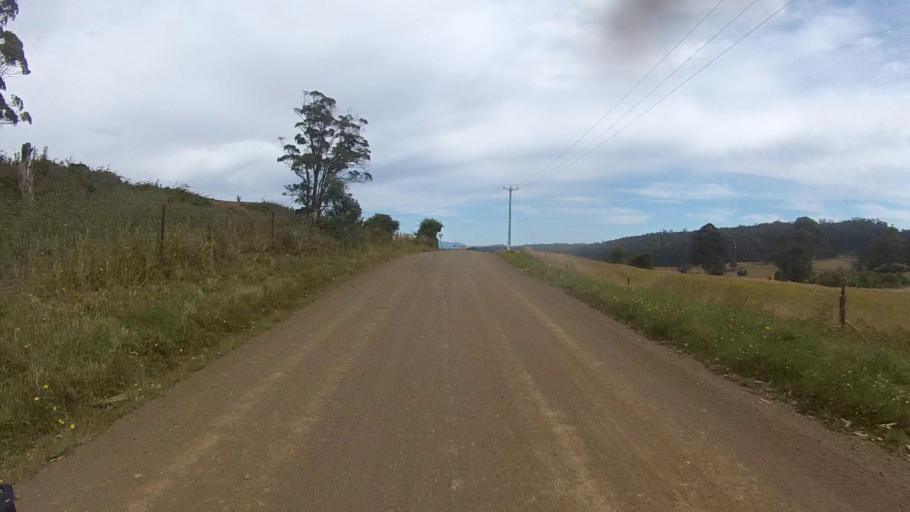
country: AU
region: Tasmania
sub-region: Sorell
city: Sorell
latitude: -42.7215
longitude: 147.7512
